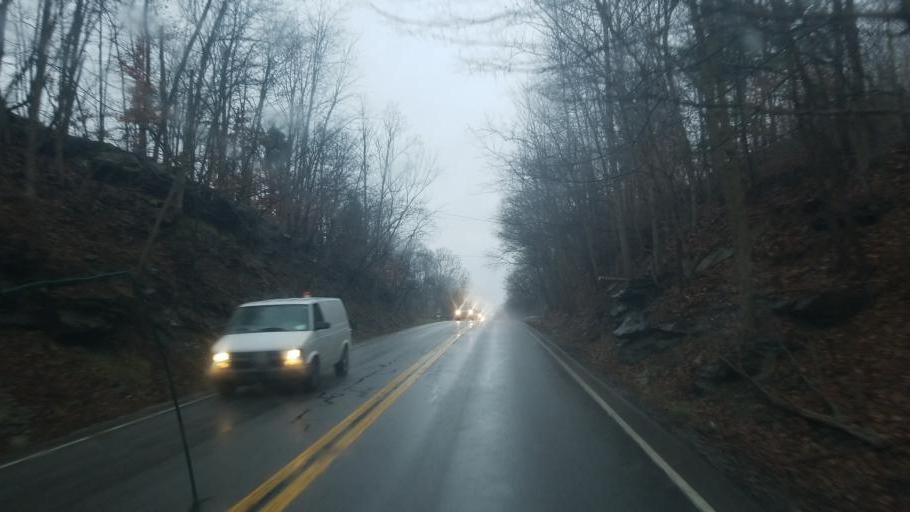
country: US
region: Indiana
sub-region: Brown County
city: Nashville
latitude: 39.1782
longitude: -86.2697
